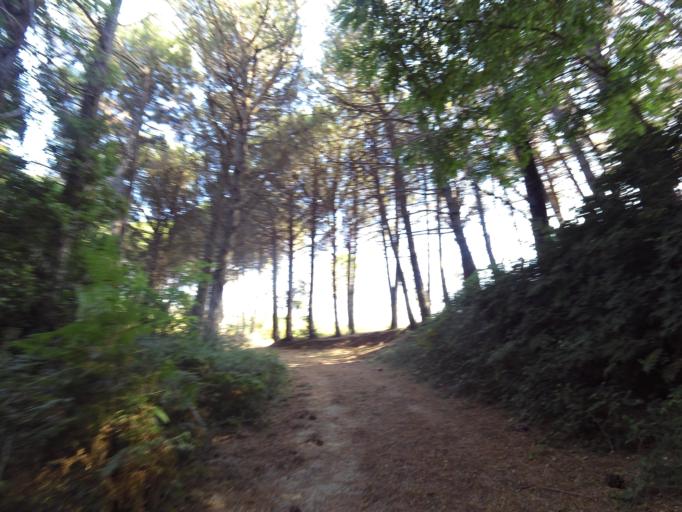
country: IT
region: Calabria
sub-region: Provincia di Reggio Calabria
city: Pazzano
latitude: 38.4677
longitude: 16.4136
